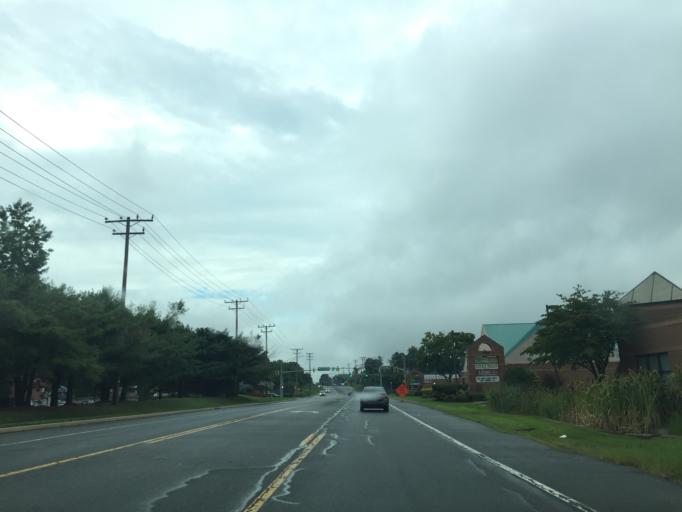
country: US
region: Maryland
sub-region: Harford County
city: Bel Air South
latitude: 39.4966
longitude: -76.3245
